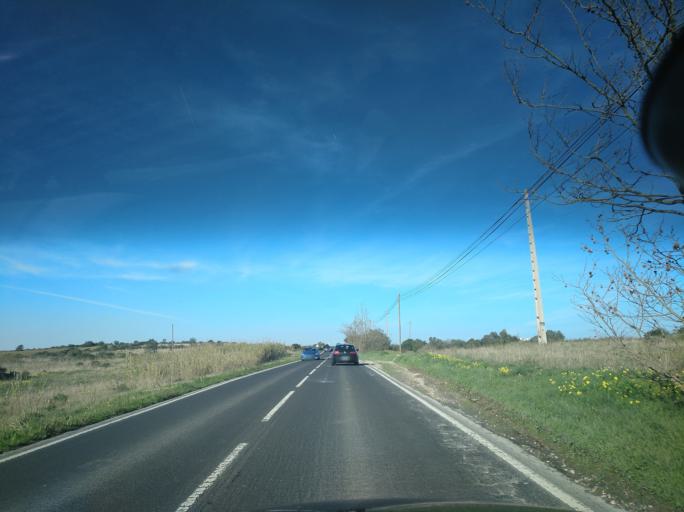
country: PT
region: Lisbon
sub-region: Mafra
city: Mafra
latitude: 38.9067
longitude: -9.3292
